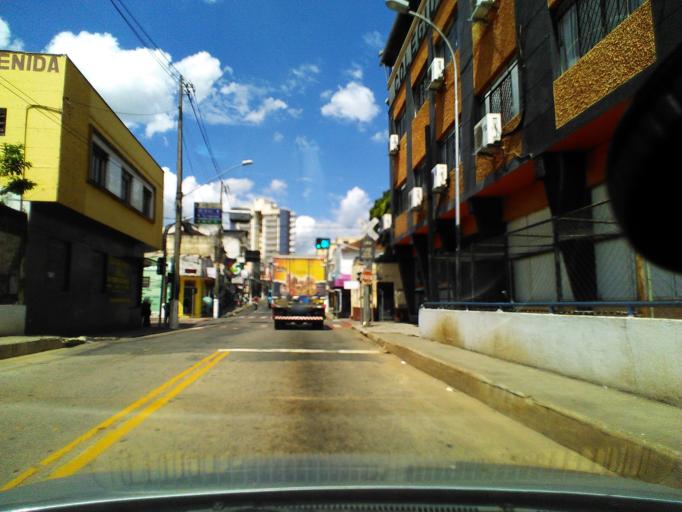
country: BR
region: Minas Gerais
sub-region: Tres Coracoes
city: Tres Coracoes
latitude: -21.6995
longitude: -45.2587
